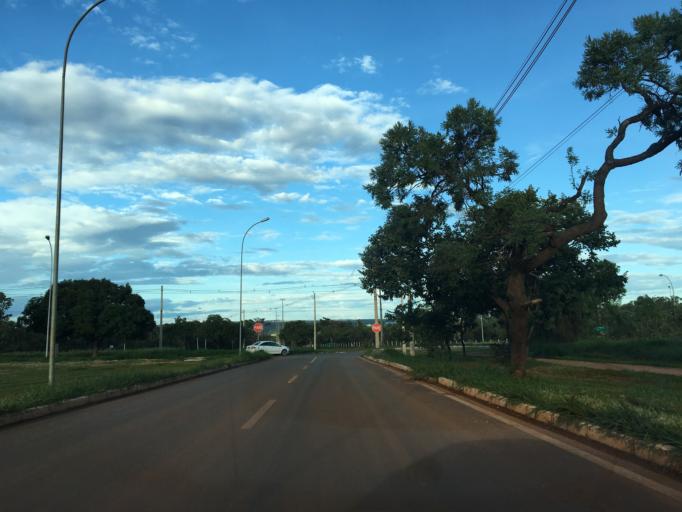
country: BR
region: Federal District
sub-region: Brasilia
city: Brasilia
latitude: -15.8075
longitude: -47.8392
